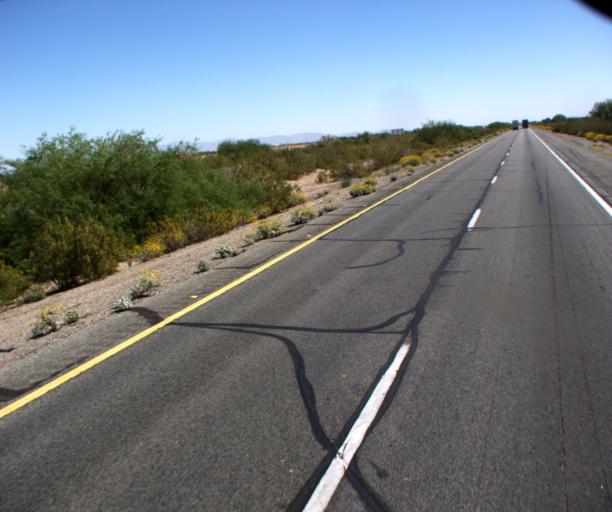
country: US
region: Arizona
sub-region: Maricopa County
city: Buckeye
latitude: 33.4862
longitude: -112.8878
